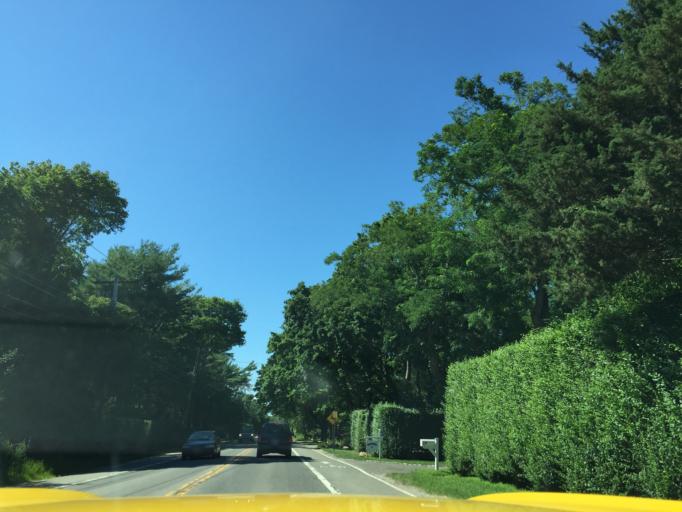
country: US
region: New York
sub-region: Suffolk County
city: Sag Harbor
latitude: 41.0068
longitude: -72.3025
